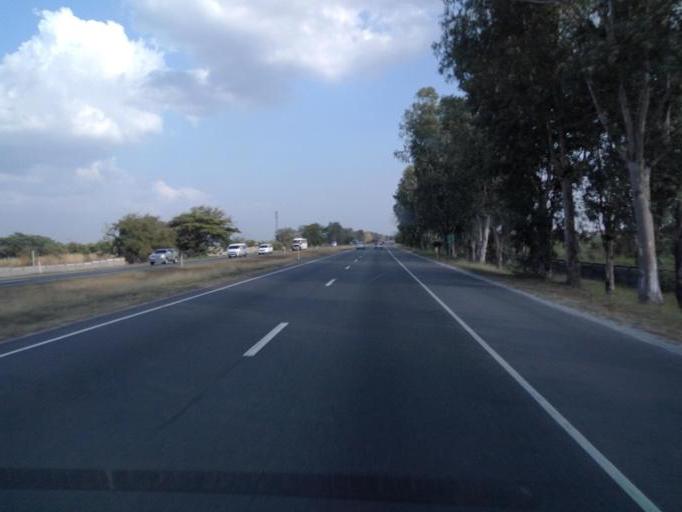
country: PH
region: Central Luzon
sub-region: Province of Pampanga
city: Acli
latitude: 15.1210
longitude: 120.6519
